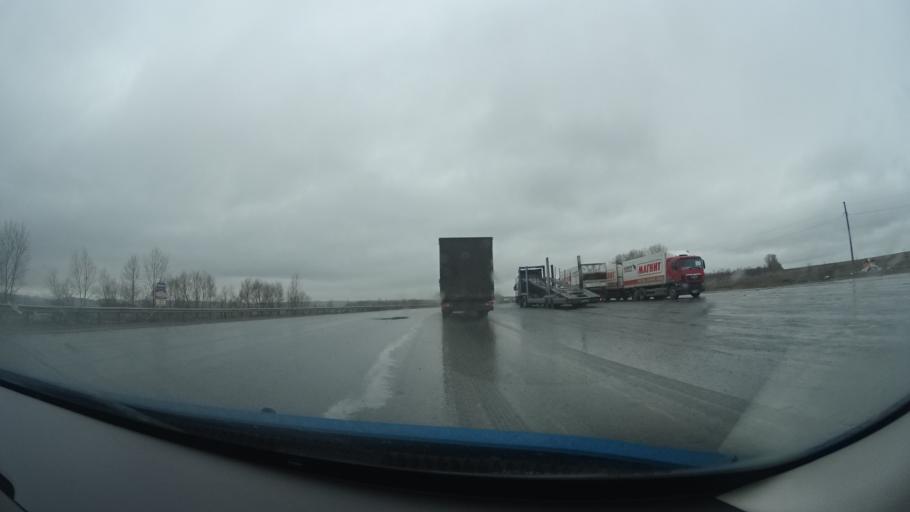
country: RU
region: Bashkortostan
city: Kandry
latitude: 54.5189
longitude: 54.0529
